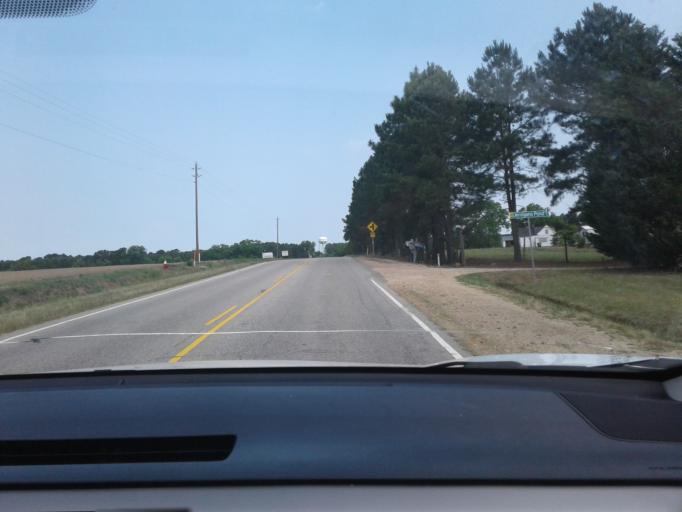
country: US
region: North Carolina
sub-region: Harnett County
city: Coats
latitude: 35.3891
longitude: -78.6668
